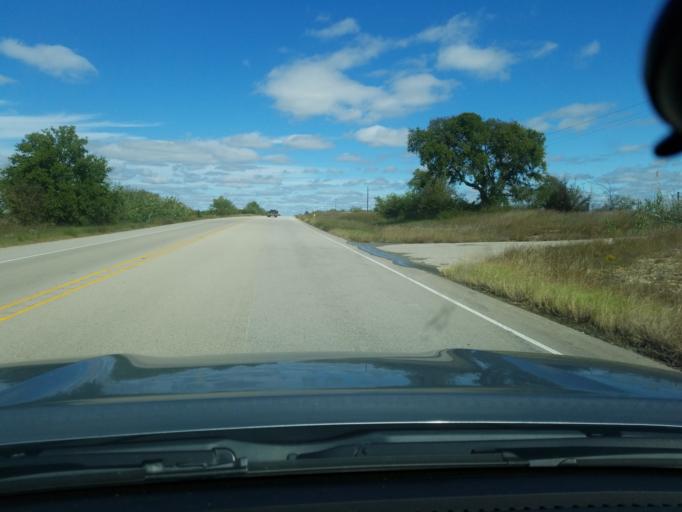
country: US
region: Texas
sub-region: Hamilton County
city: Hamilton
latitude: 31.6578
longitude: -98.1433
